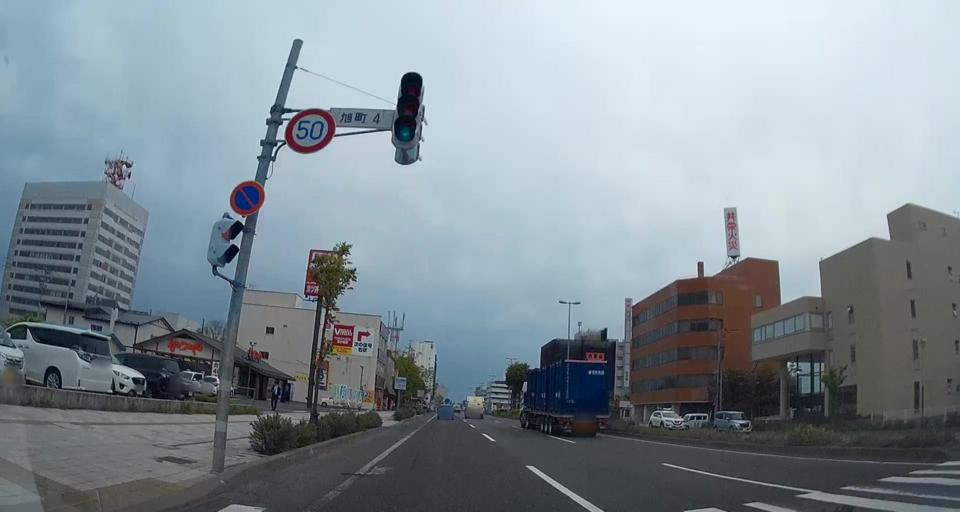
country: JP
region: Hokkaido
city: Tomakomai
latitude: 42.6356
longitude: 141.6061
